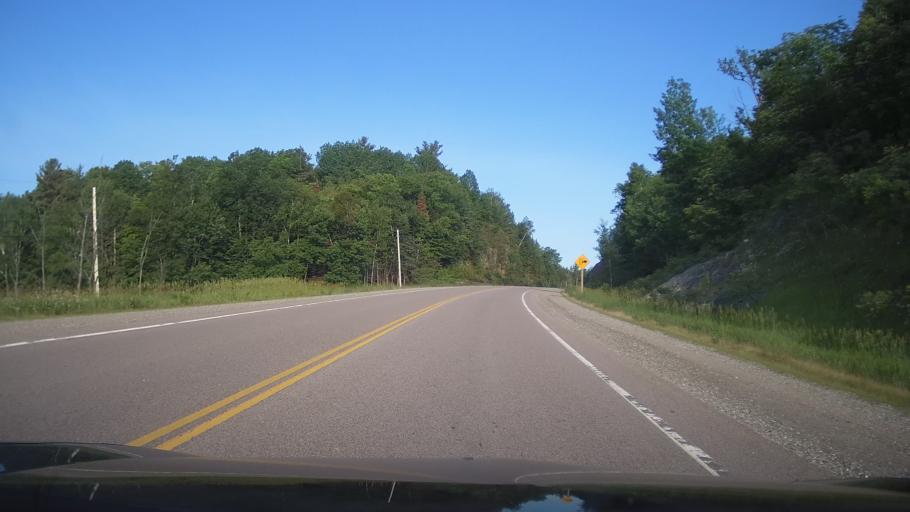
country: CA
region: Ontario
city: Skatepark
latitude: 44.7515
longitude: -76.8331
